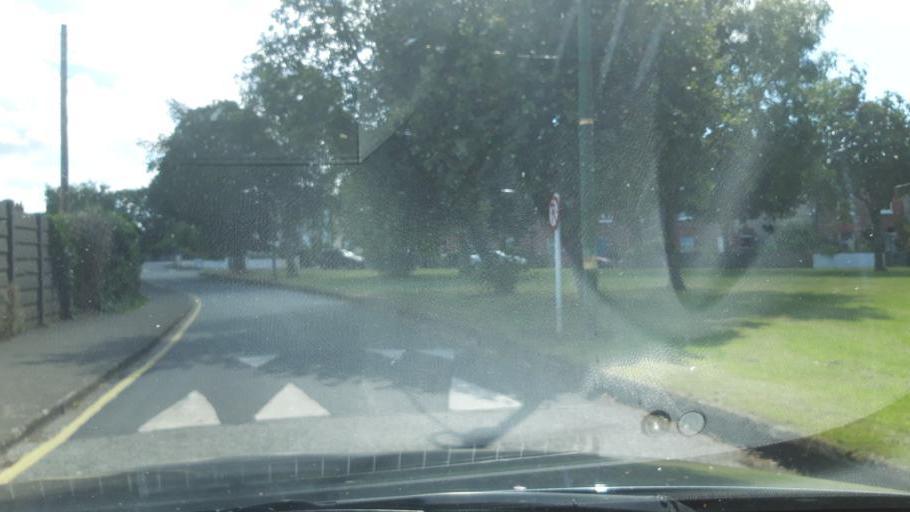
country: IE
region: Leinster
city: Crumlin
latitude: 53.3400
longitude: -6.3262
